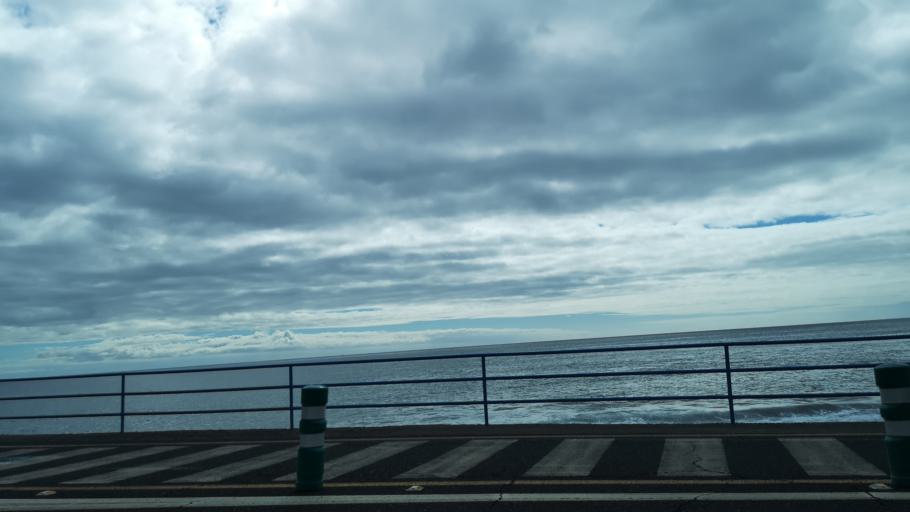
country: ES
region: Canary Islands
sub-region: Provincia de Santa Cruz de Tenerife
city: Alajero
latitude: 28.0835
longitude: -17.3358
